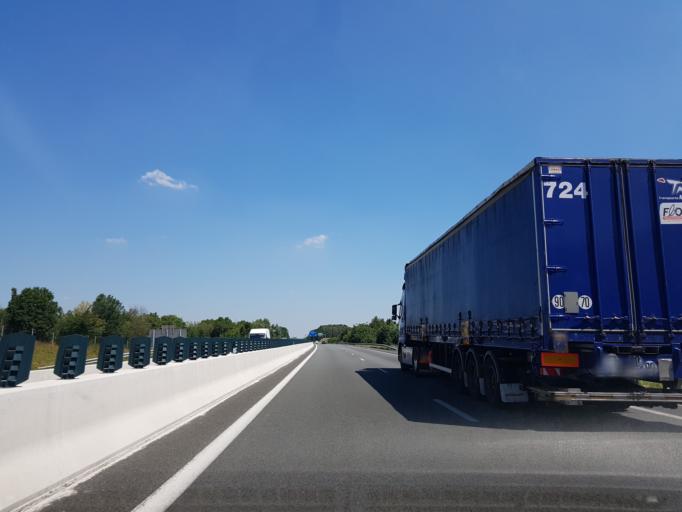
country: FR
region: Nord-Pas-de-Calais
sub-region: Departement du Nord
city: Raillencourt-Sainte-Olle
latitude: 50.1700
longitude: 3.1788
